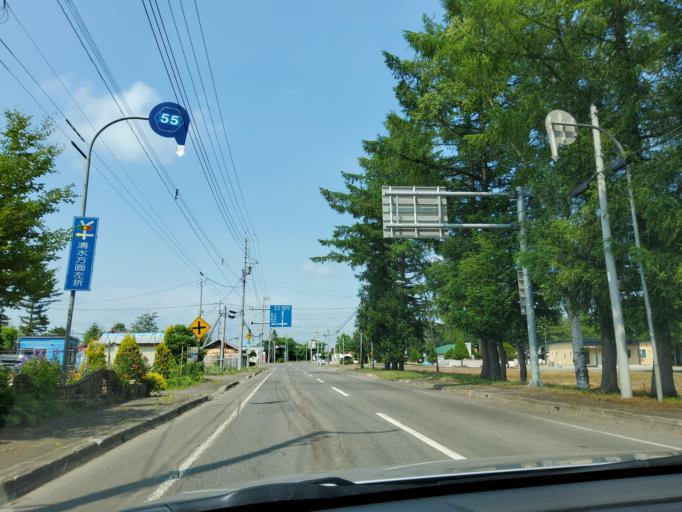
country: JP
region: Hokkaido
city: Obihiro
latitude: 42.8644
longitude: 143.0146
